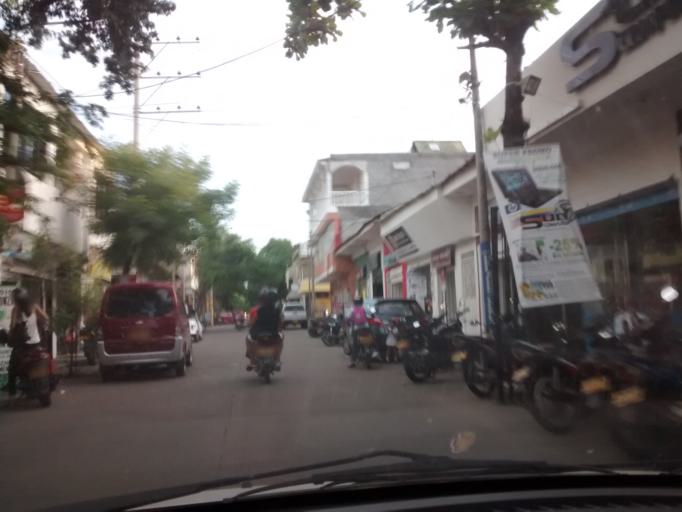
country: CO
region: Cundinamarca
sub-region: Girardot
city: Girardot City
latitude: 4.3003
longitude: -74.8054
